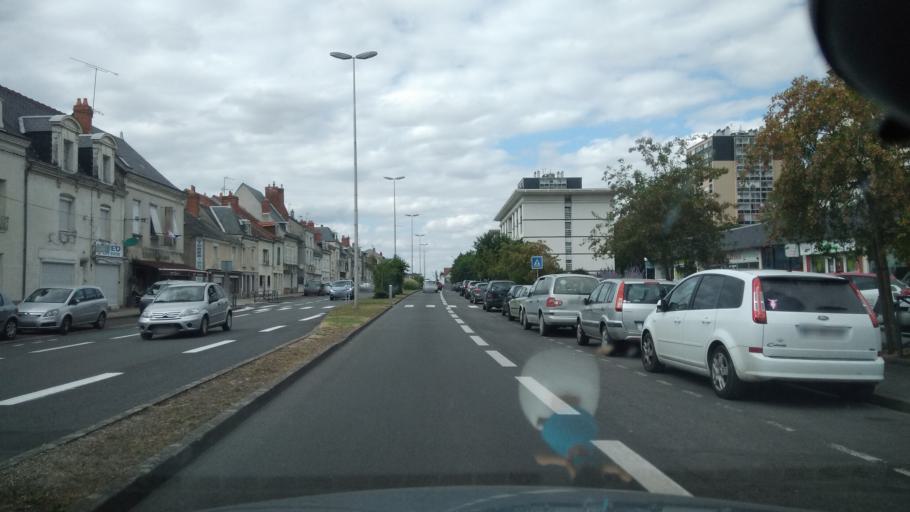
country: FR
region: Poitou-Charentes
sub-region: Departement de la Vienne
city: Chatellerault
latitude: 46.8220
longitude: 0.5446
